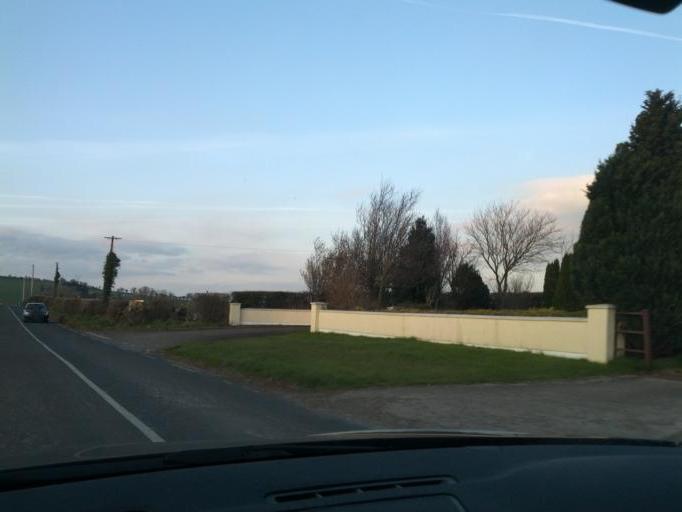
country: IE
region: Munster
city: Nenagh Bridge
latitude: 52.9051
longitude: -8.2112
